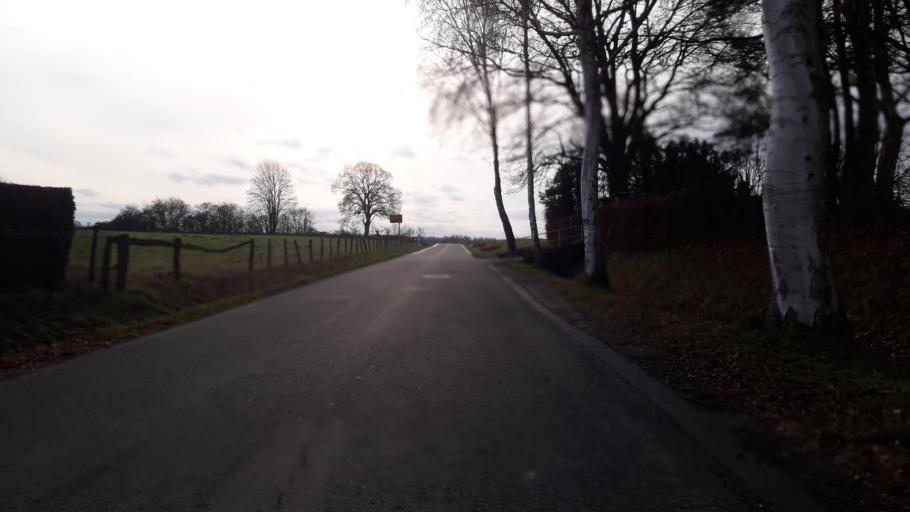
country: DE
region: North Rhine-Westphalia
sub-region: Regierungsbezirk Arnsberg
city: Soest
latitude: 51.5817
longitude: 8.0580
